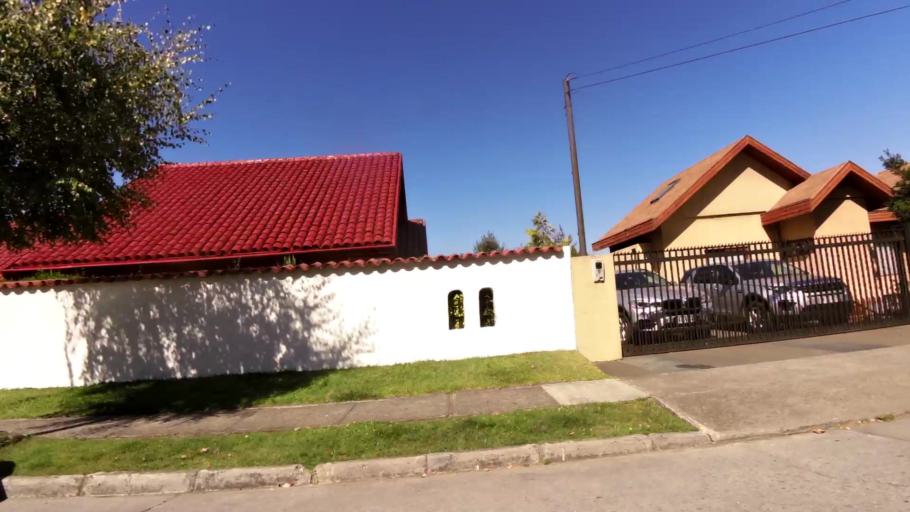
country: CL
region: Biobio
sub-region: Provincia de Concepcion
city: Concepcion
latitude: -36.7928
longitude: -73.0588
